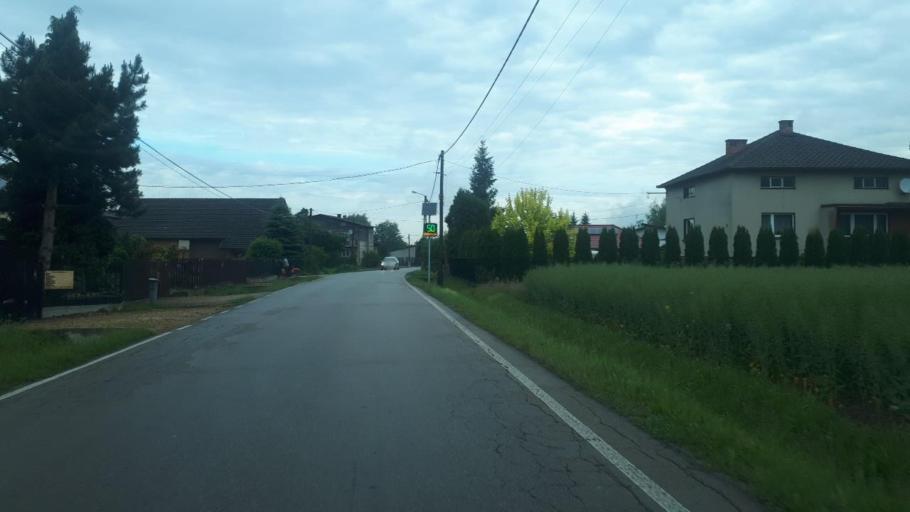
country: PL
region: Silesian Voivodeship
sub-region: Powiat bielski
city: Wilamowice
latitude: 49.9467
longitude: 19.1476
